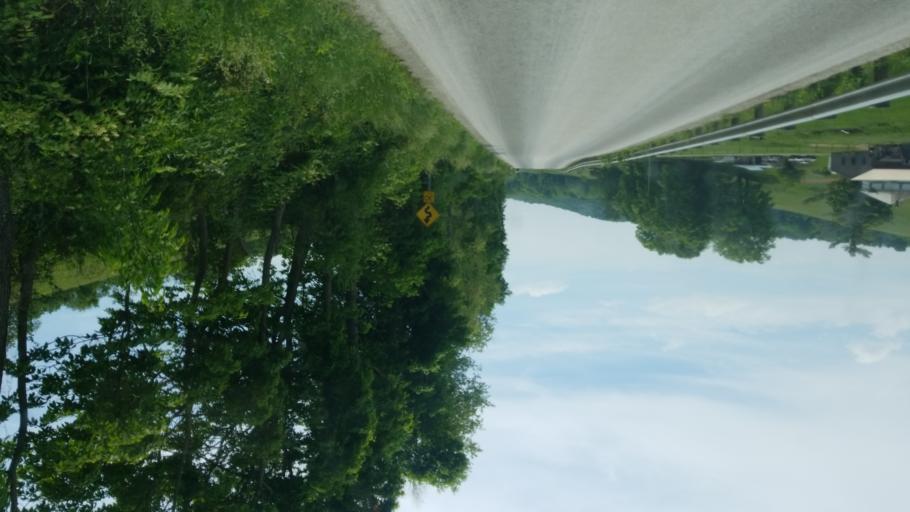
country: US
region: Ohio
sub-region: Coshocton County
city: West Lafayette
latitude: 40.4144
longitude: -81.7735
